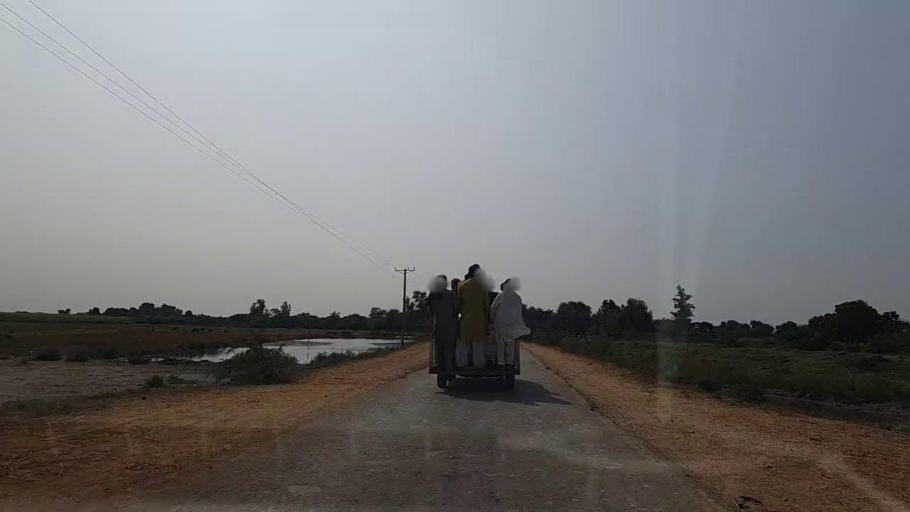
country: PK
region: Sindh
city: Chuhar Jamali
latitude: 24.3718
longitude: 67.9670
